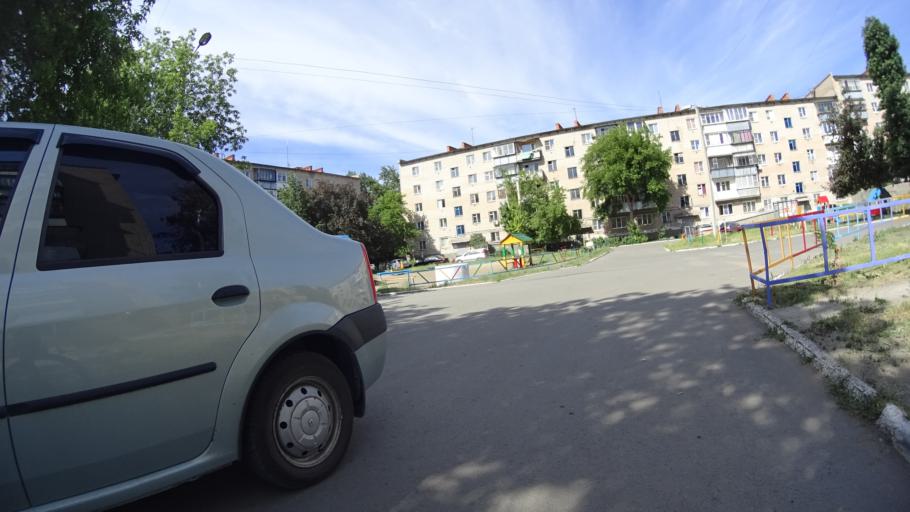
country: RU
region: Chelyabinsk
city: Troitsk
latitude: 54.0510
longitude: 61.6372
